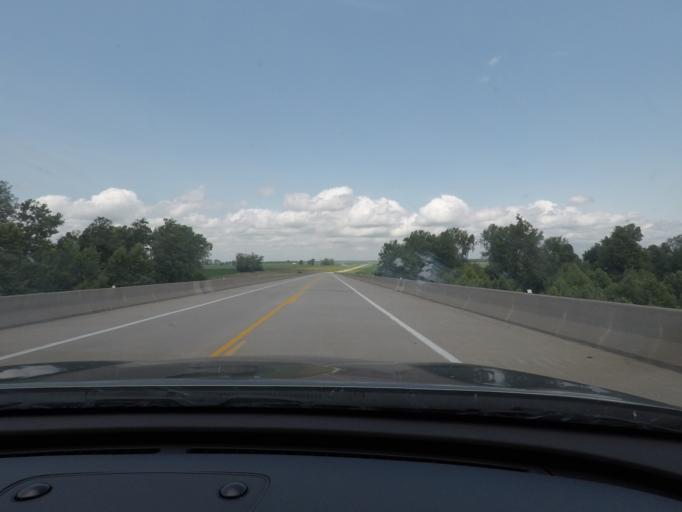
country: US
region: Missouri
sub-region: Carroll County
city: Carrollton
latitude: 39.2169
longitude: -93.5122
